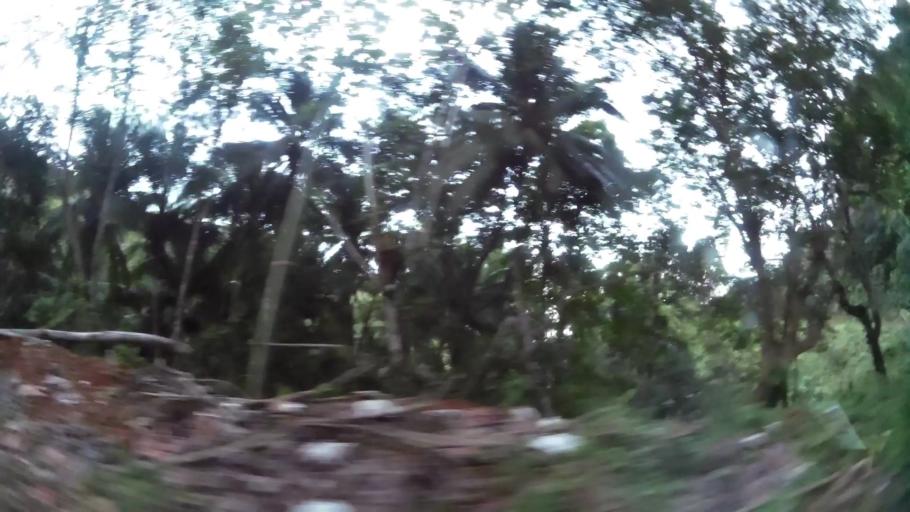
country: DM
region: Saint Andrew
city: Calibishie
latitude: 15.5928
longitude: -61.3581
